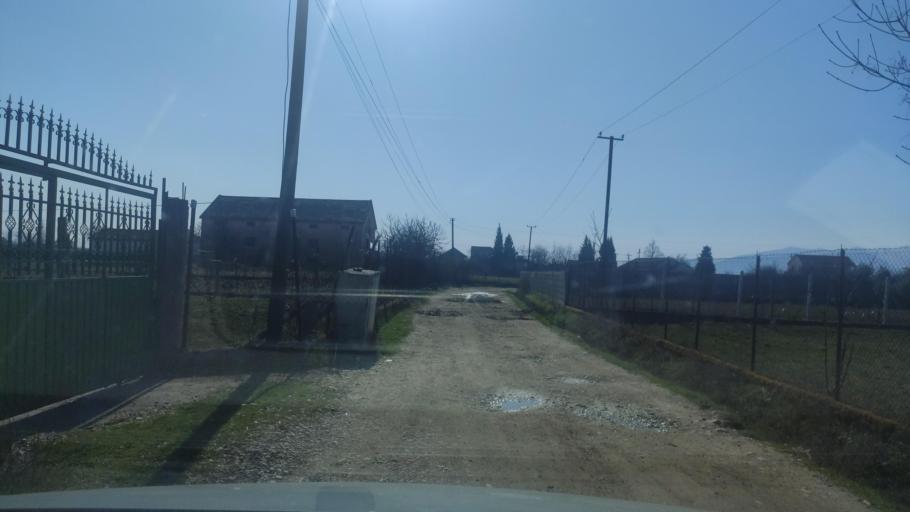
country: AL
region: Shkoder
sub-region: Rrethi i Malesia e Madhe
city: Grude-Fushe
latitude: 42.1628
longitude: 19.4577
